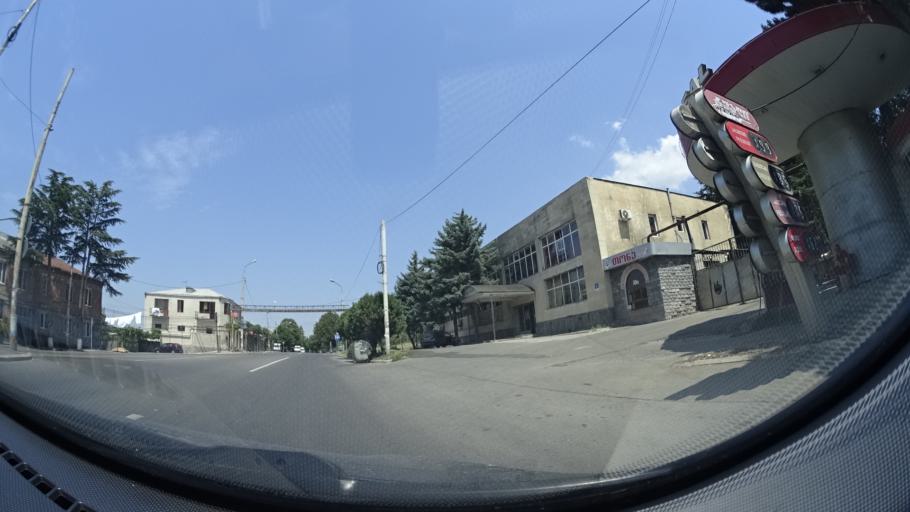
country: GE
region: Shida Kartli
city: Gori
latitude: 41.9928
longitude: 44.1220
